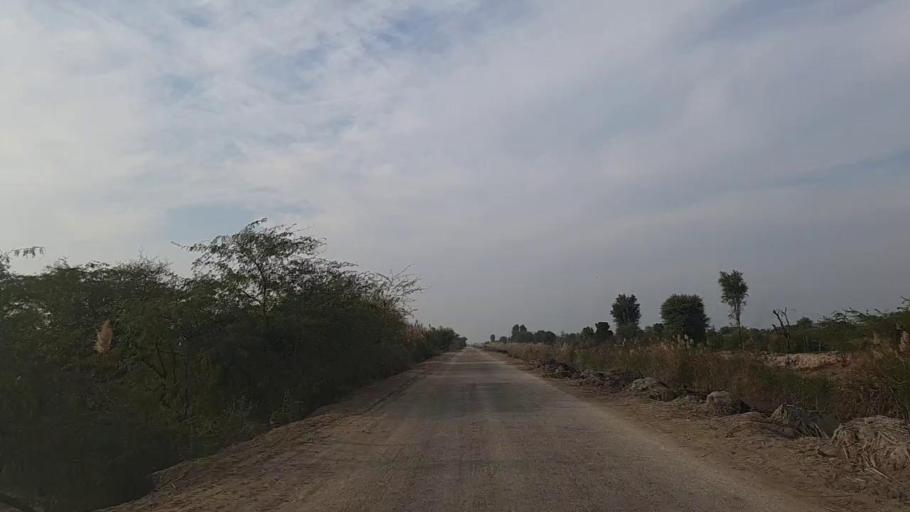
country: PK
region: Sindh
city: Daur
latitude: 26.4931
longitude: 68.4554
